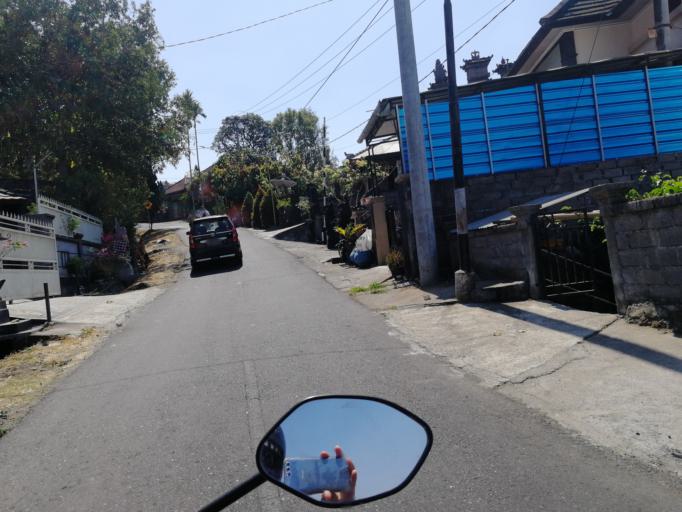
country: ID
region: Bali
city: Banjar Kedisan
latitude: -8.1458
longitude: 115.3076
